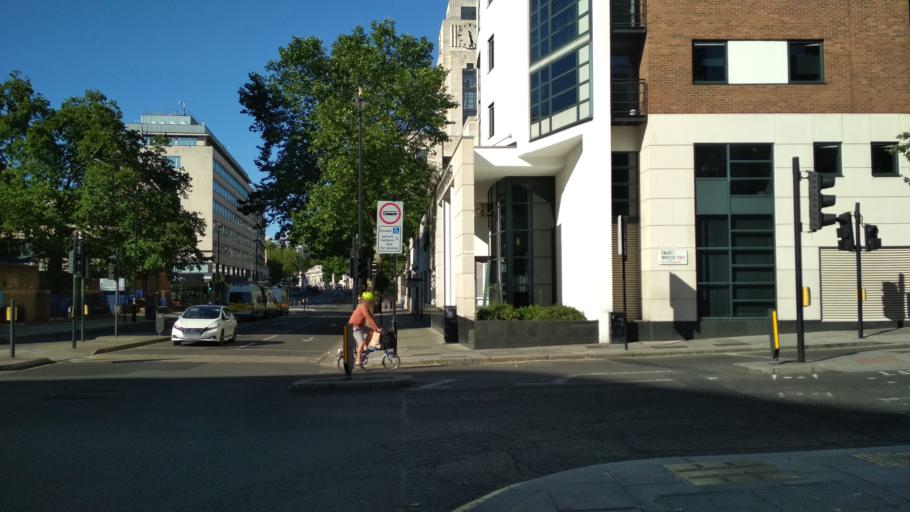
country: GB
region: England
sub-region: Greater London
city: Battersea
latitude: 51.4907
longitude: -0.1499
